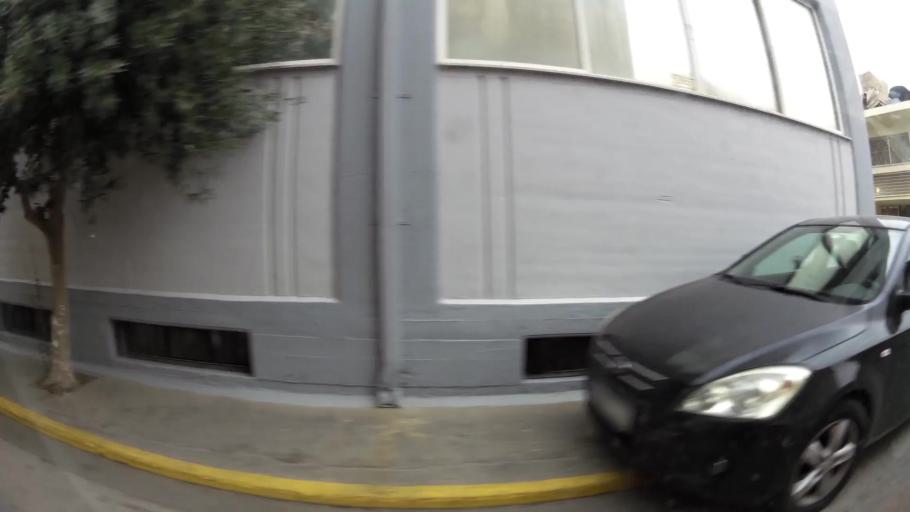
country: GR
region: Attica
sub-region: Nomarchia Athinas
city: Peristeri
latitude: 38.0021
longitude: 23.6963
